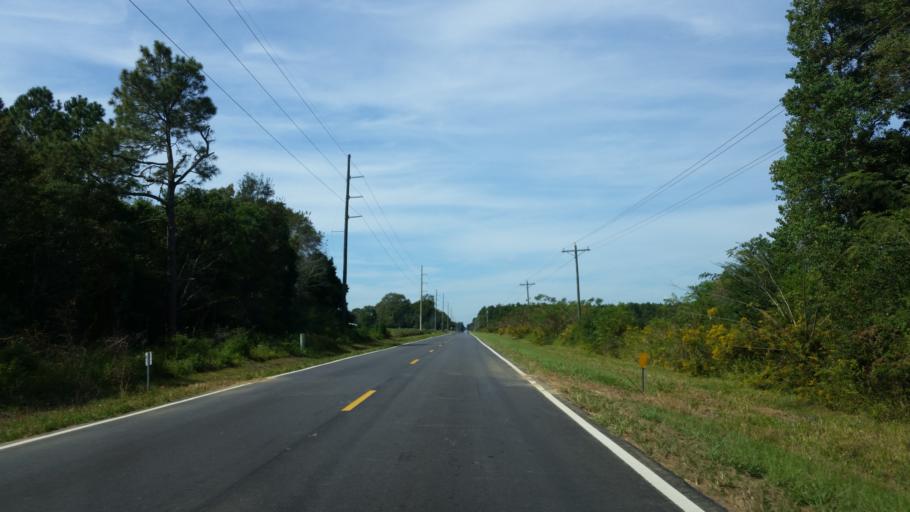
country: US
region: Alabama
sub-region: Baldwin County
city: Loxley
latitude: 30.6332
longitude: -87.6866
